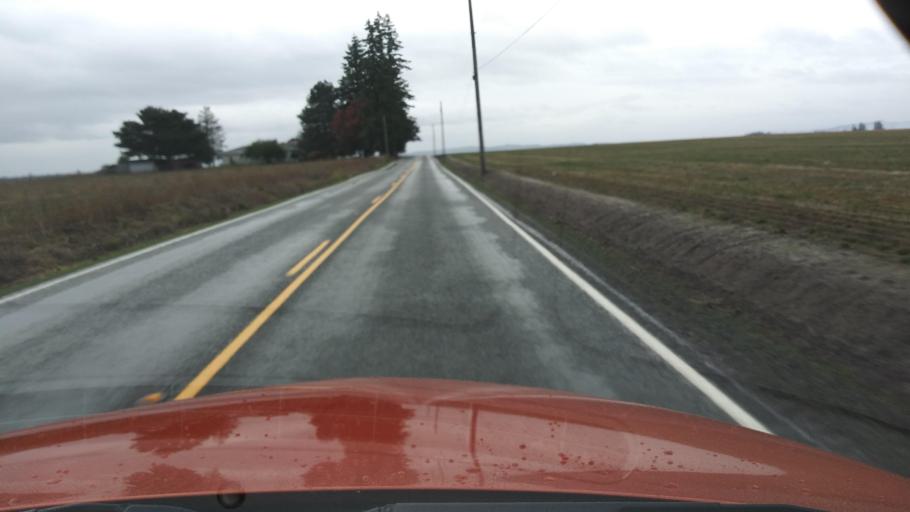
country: US
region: Oregon
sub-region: Washington County
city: North Plains
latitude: 45.5862
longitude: -123.0173
